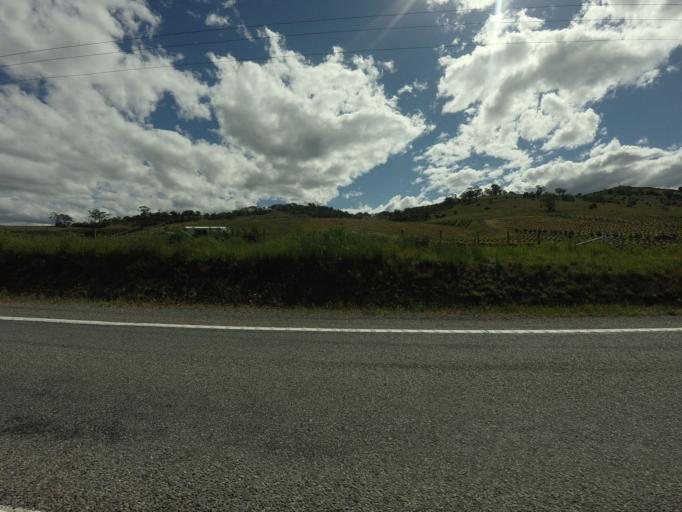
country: AU
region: Tasmania
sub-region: Northern Midlands
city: Evandale
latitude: -42.0585
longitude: 147.4828
